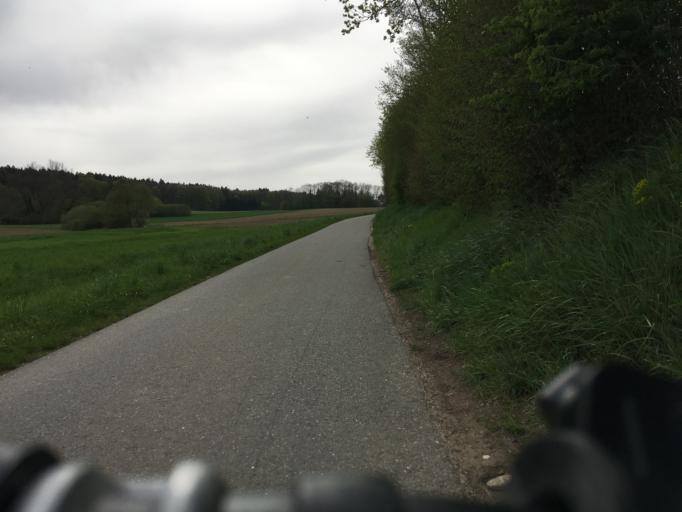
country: DE
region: Baden-Wuerttemberg
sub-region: Freiburg Region
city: Gailingen
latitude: 47.7125
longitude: 8.7611
